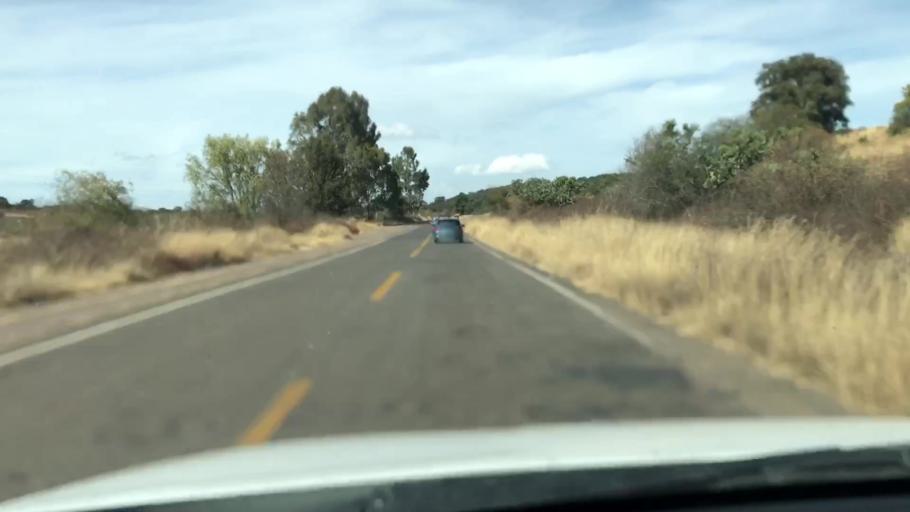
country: MX
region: Jalisco
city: Chiquilistlan
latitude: 20.1854
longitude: -103.7244
